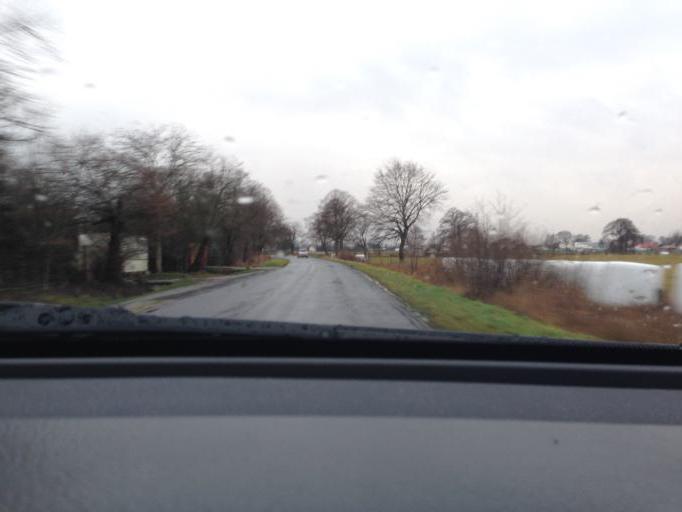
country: PL
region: Opole Voivodeship
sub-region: Powiat opolski
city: Wegry
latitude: 50.7304
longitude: 18.0581
